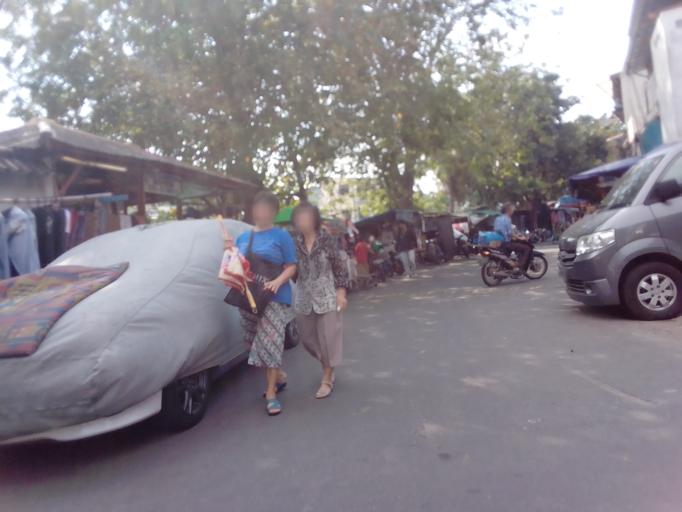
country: ID
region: Jakarta Raya
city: Jakarta
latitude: -6.1454
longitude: 106.8110
